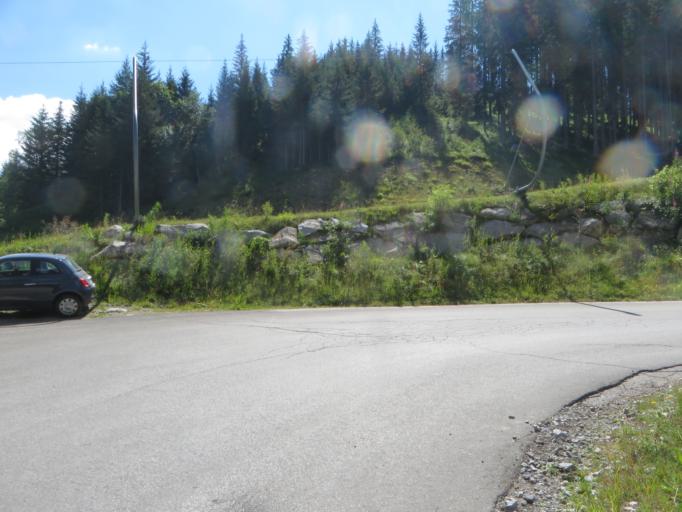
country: IT
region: Trentino-Alto Adige
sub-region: Provincia di Trento
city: Mezzana
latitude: 46.2349
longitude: 10.8167
